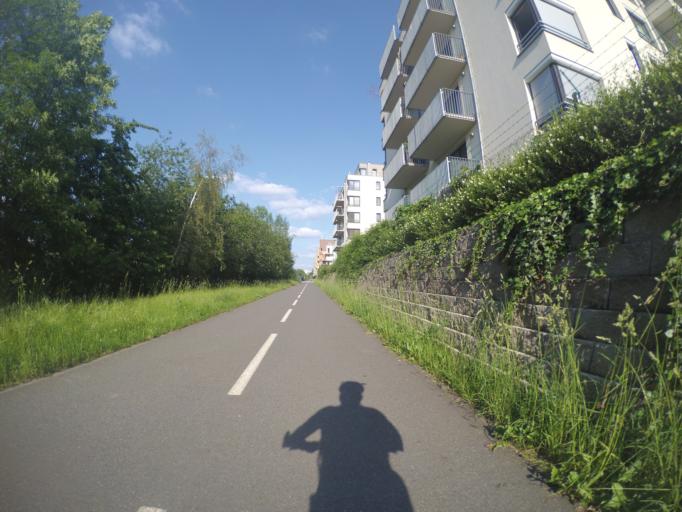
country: CZ
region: Praha
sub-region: Praha 9
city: Vysocany
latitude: 50.1055
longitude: 14.5183
